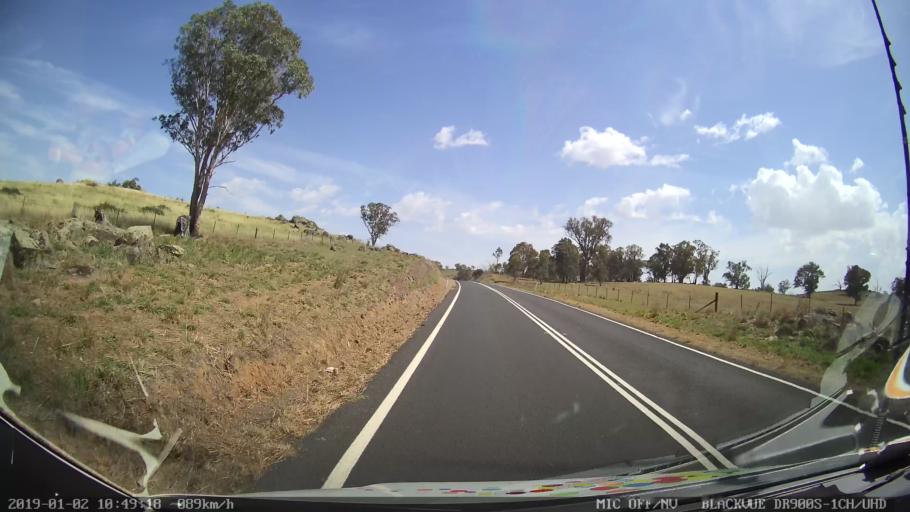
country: AU
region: New South Wales
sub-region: Cootamundra
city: Cootamundra
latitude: -34.7261
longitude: 148.2771
